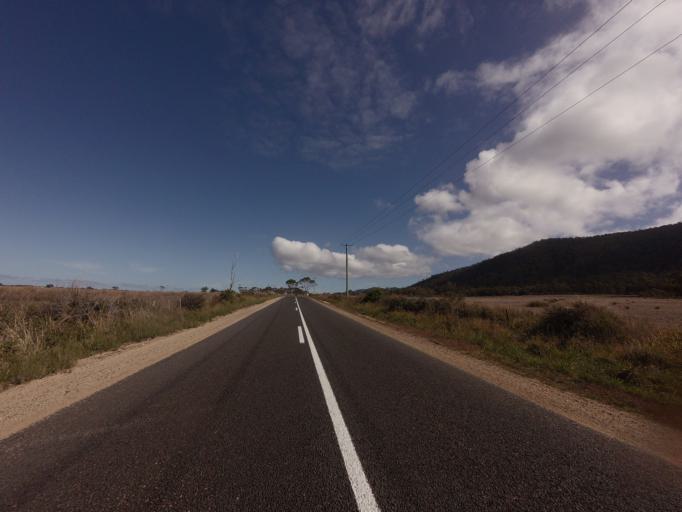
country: AU
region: Tasmania
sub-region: Break O'Day
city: St Helens
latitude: -41.7298
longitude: 148.2740
